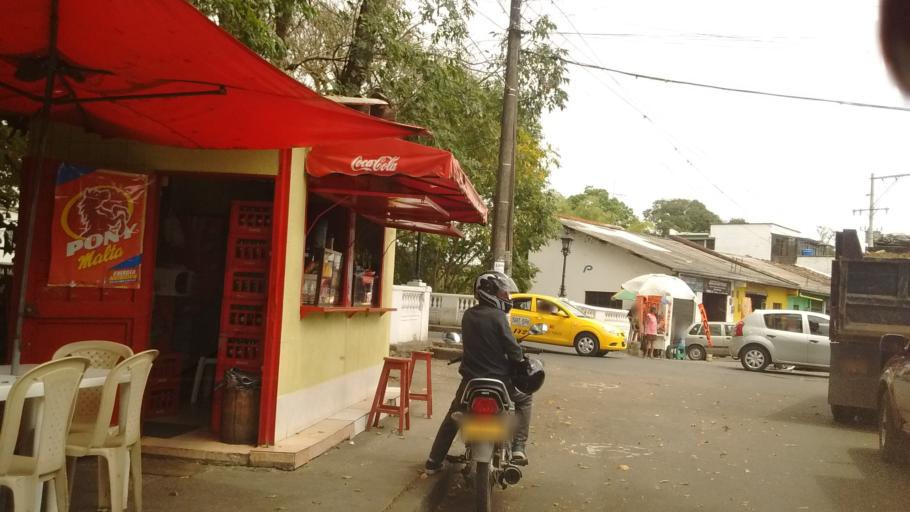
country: CO
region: Cauca
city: Popayan
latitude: 2.4450
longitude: -76.6065
